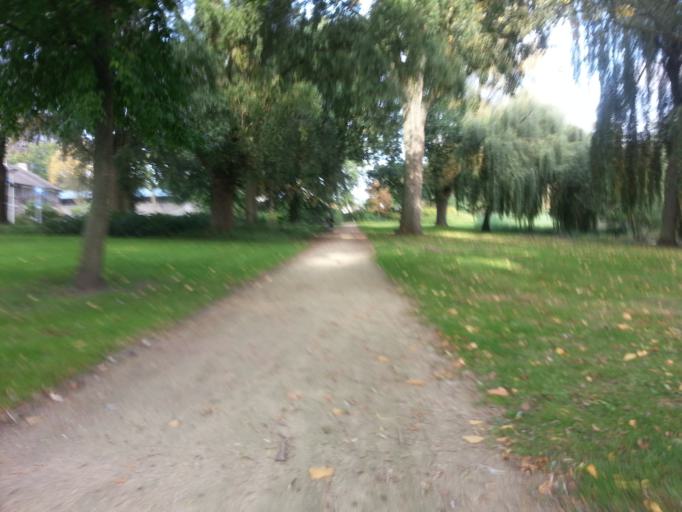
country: NL
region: North Brabant
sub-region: Gemeente Eindhoven
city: Villapark
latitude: 51.4651
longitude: 5.4918
